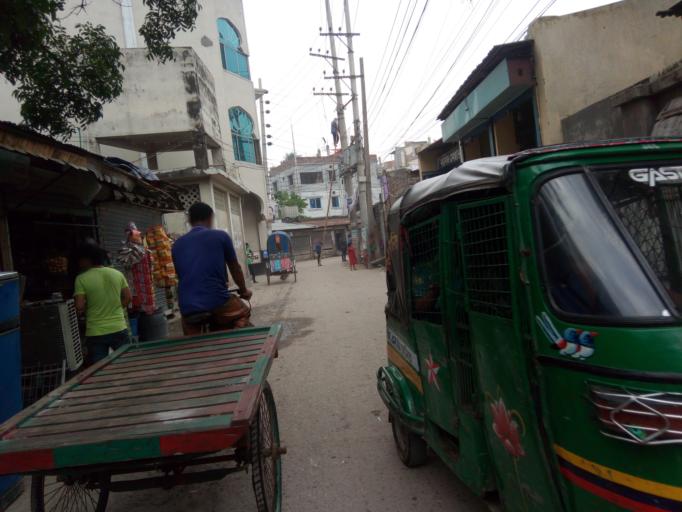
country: BD
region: Dhaka
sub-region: Dhaka
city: Dhaka
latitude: 23.6863
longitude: 90.4445
